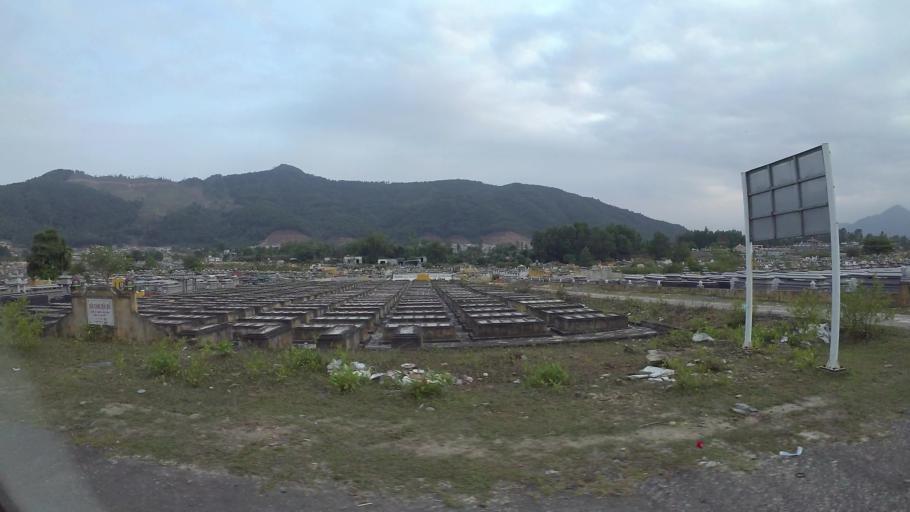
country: VN
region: Da Nang
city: Lien Chieu
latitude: 16.0618
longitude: 108.1214
